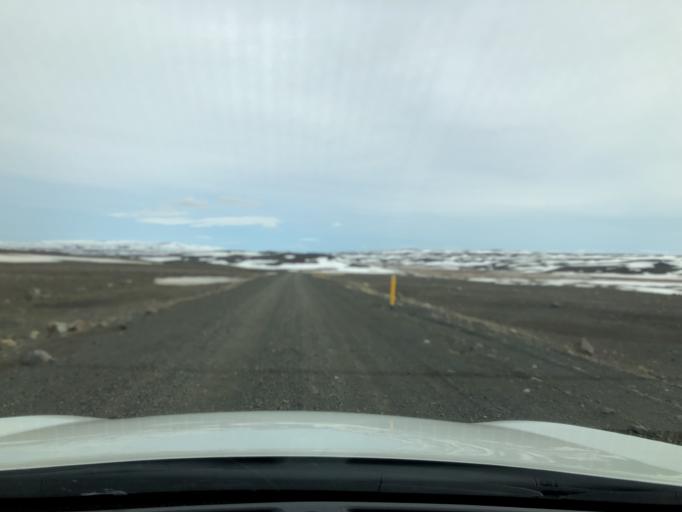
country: IS
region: East
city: Egilsstadir
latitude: 65.2930
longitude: -15.4536
